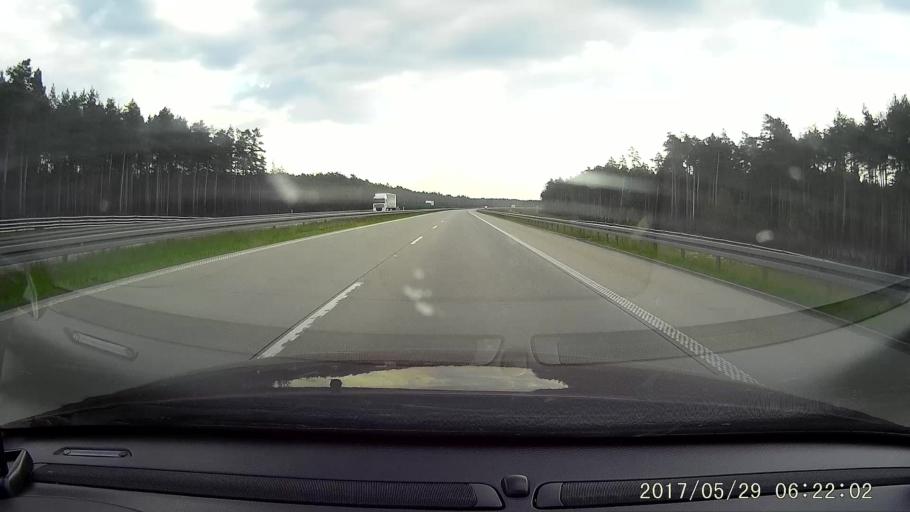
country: PL
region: Lower Silesian Voivodeship
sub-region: Powiat boleslawiecki
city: Boleslawiec
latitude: 51.3091
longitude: 15.5337
